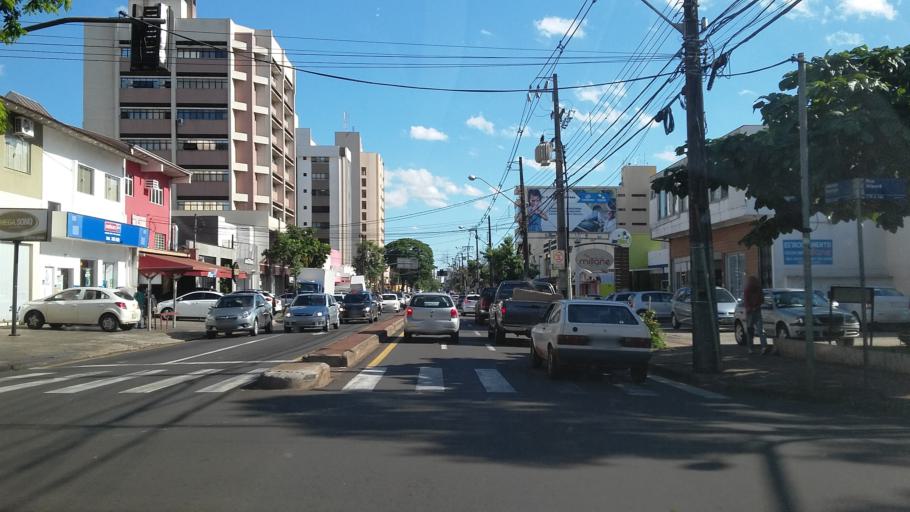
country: BR
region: Parana
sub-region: Londrina
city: Londrina
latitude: -23.3062
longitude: -51.1785
